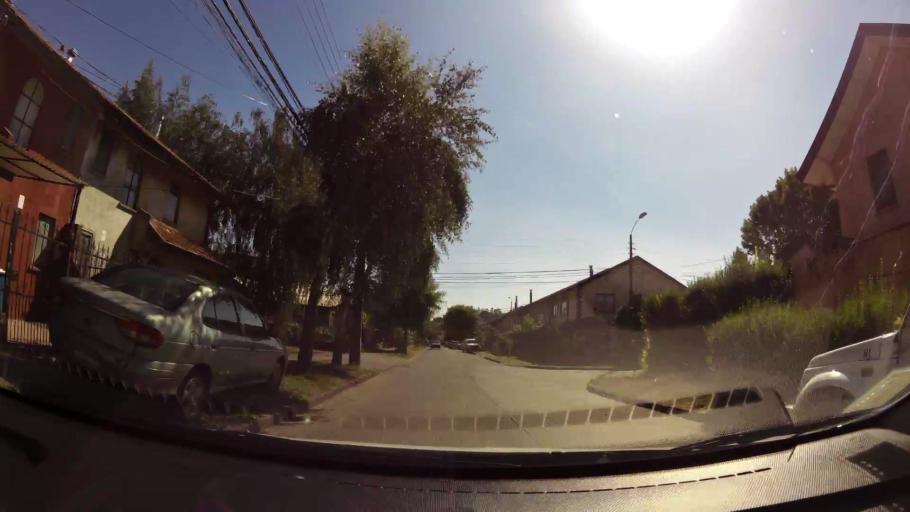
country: CL
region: Biobio
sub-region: Provincia de Concepcion
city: Concepcion
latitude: -36.7963
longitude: -73.0515
